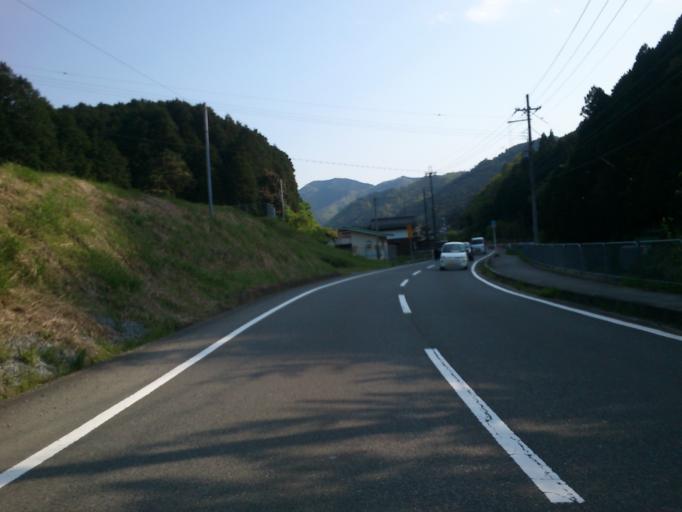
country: JP
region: Kyoto
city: Fukuchiyama
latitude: 35.2761
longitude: 135.0716
